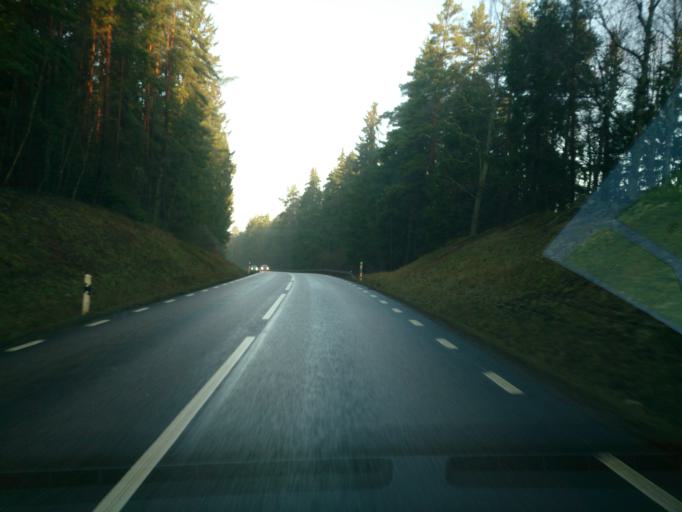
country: SE
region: OEstergoetland
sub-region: Atvidabergs Kommun
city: Atvidaberg
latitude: 58.2684
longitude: 15.9242
